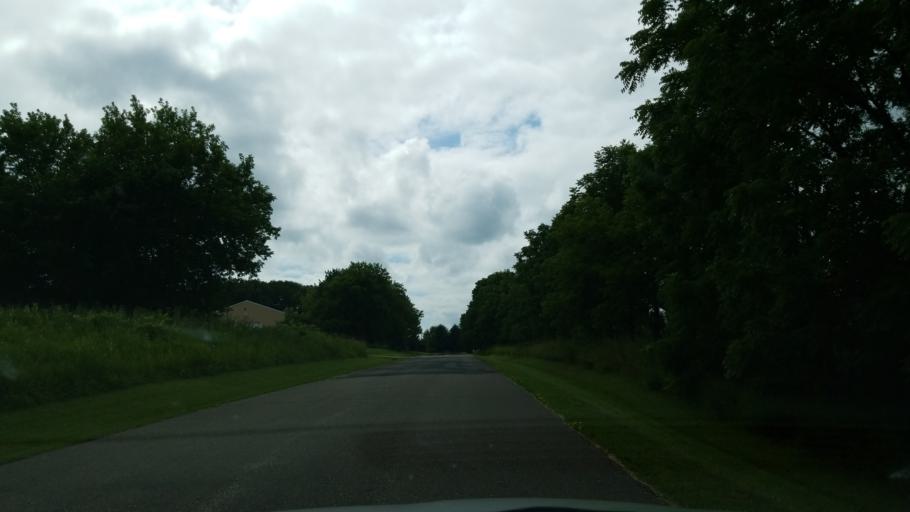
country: US
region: Wisconsin
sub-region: Saint Croix County
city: Glenwood City
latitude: 45.0096
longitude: -92.1729
